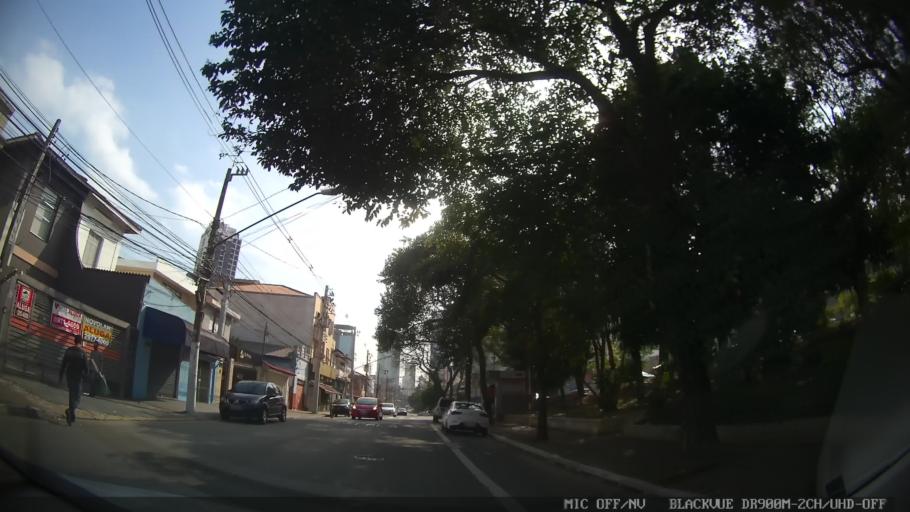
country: BR
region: Sao Paulo
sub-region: Sao Paulo
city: Sao Paulo
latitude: -23.4993
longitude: -46.6197
